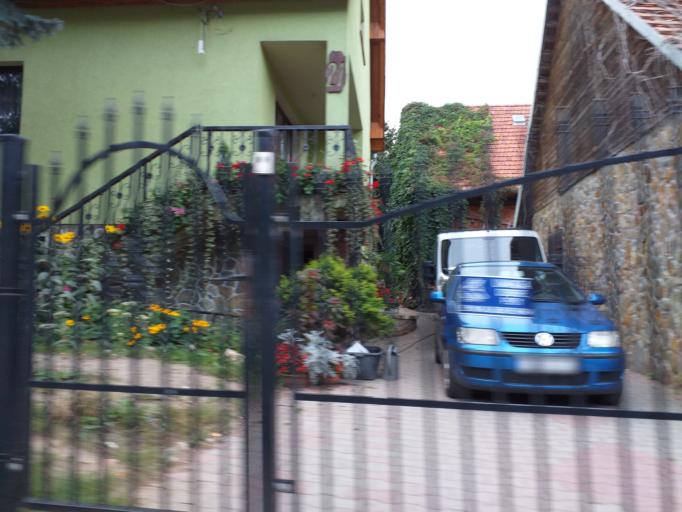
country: PL
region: Lower Silesian Voivodeship
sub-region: Powiat lubanski
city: Lesna
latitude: 51.0190
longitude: 15.3142
